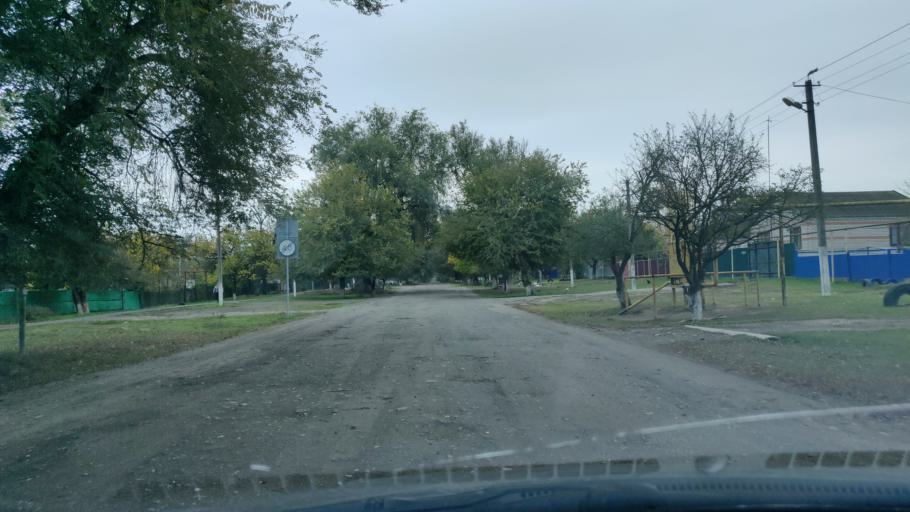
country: RU
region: Stavropol'skiy
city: Irgakly
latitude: 44.2436
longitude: 44.7206
